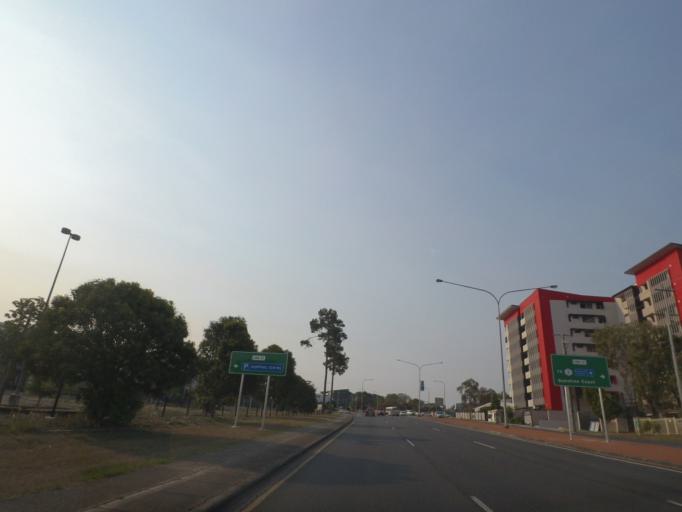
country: AU
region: Queensland
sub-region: Brisbane
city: Upper Mount Gravatt
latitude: -27.5653
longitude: 153.0873
